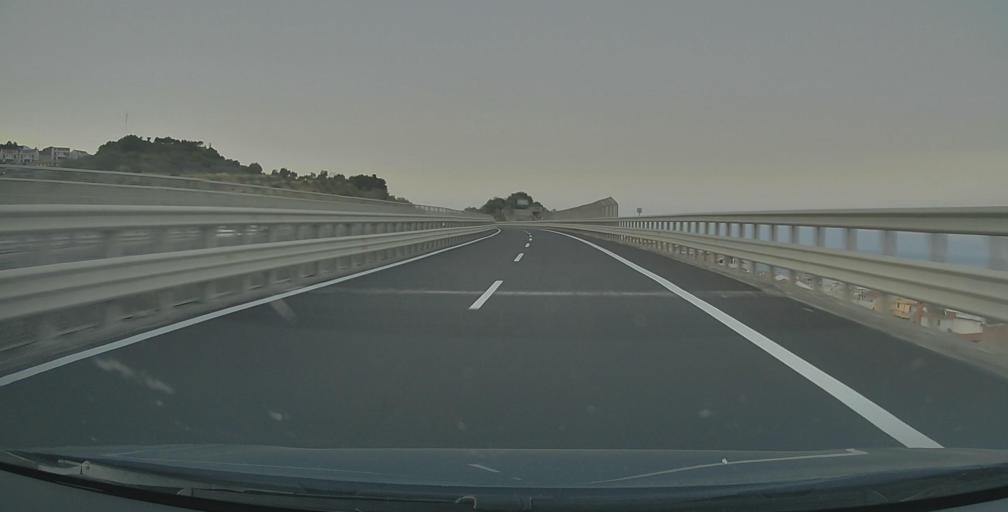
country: IT
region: Sicily
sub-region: Messina
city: Santa Teresa di Riva
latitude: 37.9411
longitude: 15.3594
